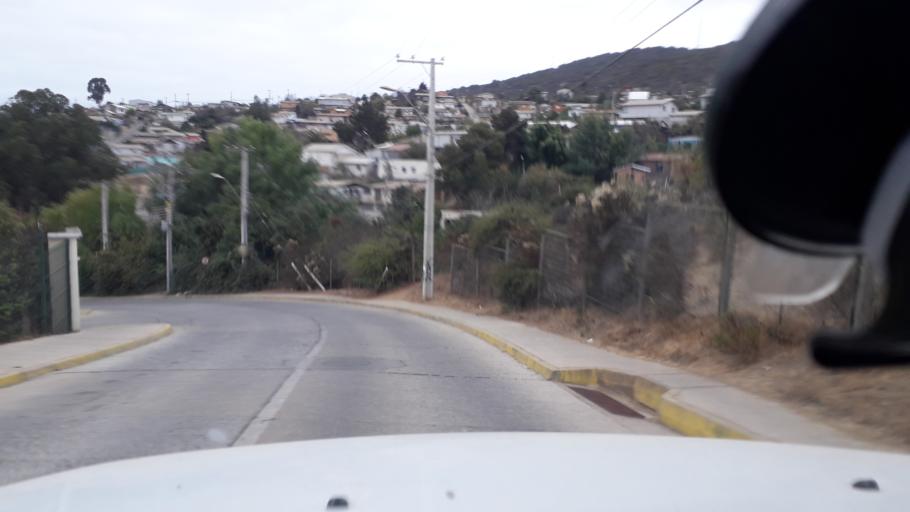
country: CL
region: Valparaiso
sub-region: Provincia de Marga Marga
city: Quilpue
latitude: -33.0327
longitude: -71.4797
